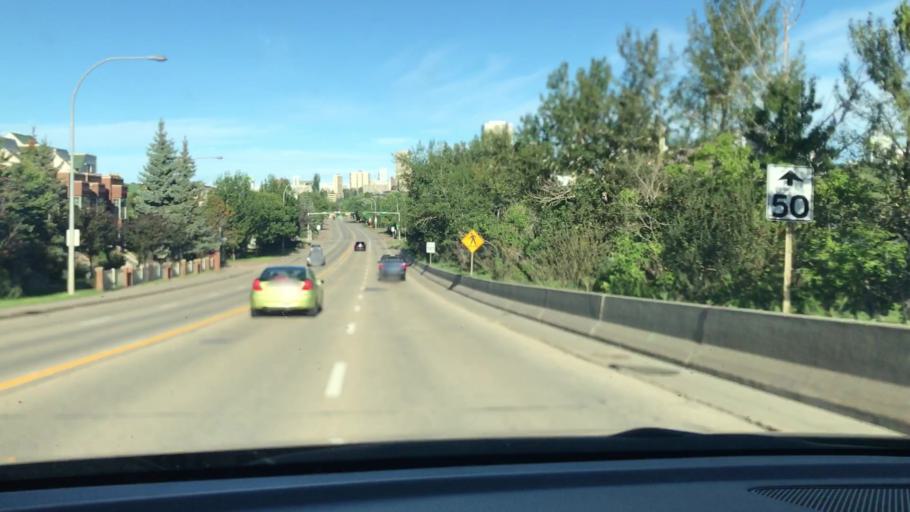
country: CA
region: Alberta
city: Edmonton
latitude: 53.5383
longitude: -113.4655
